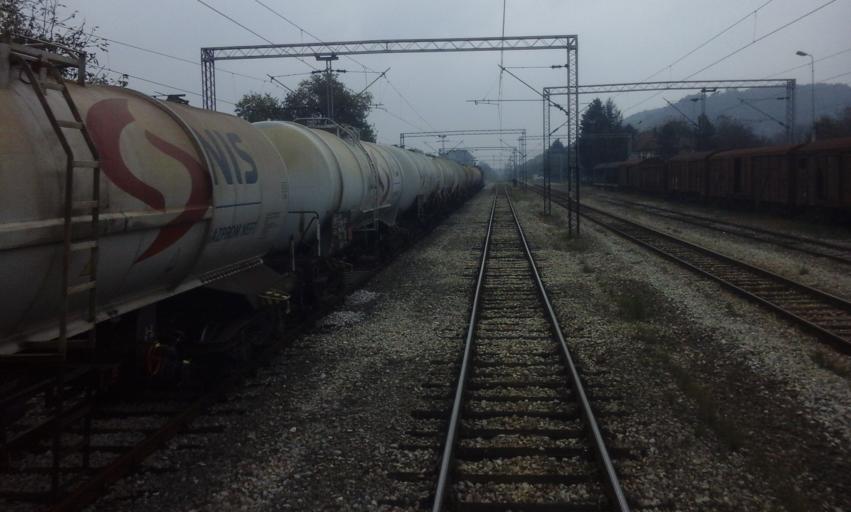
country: RS
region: Central Serbia
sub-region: Sumadijski Okrug
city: Batocina
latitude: 44.0841
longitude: 21.1786
